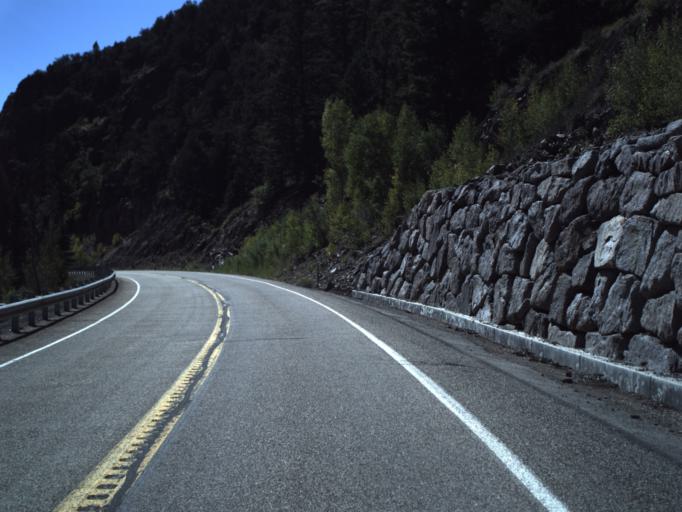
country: US
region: Utah
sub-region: Beaver County
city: Beaver
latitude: 38.2762
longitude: -112.4611
